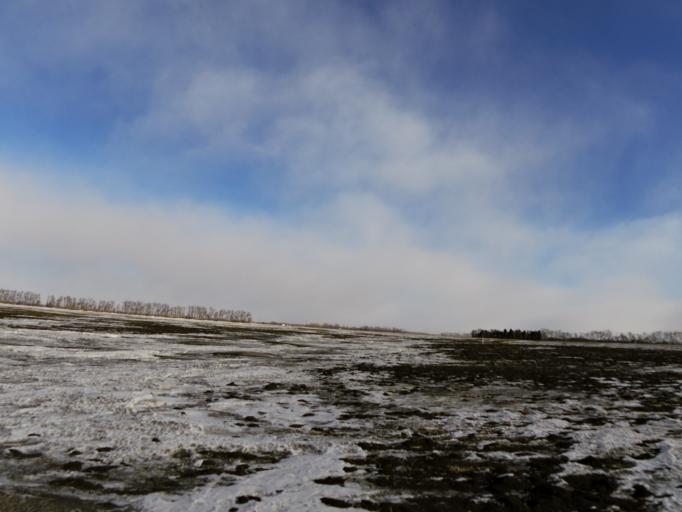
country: US
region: North Dakota
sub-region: Walsh County
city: Grafton
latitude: 48.3982
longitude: -97.2020
